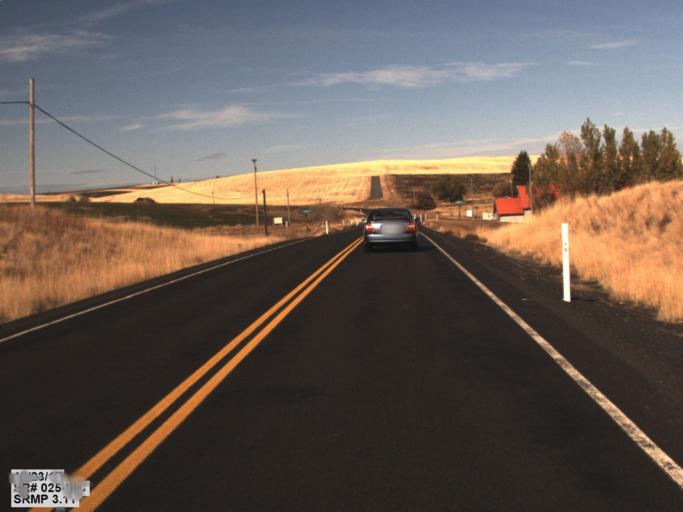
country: US
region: Washington
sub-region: Lincoln County
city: Davenport
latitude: 47.6998
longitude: -118.1410
